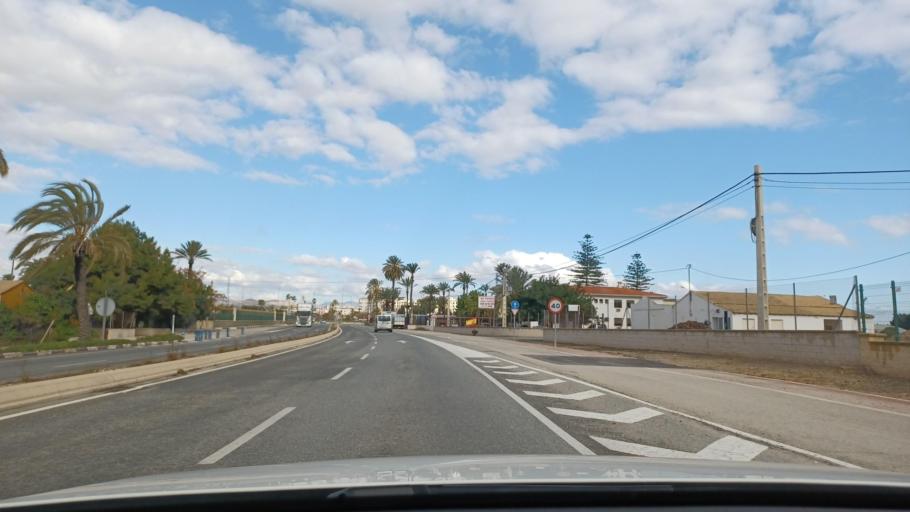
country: ES
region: Valencia
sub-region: Provincia de Alicante
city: Elche
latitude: 38.2464
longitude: -0.6984
